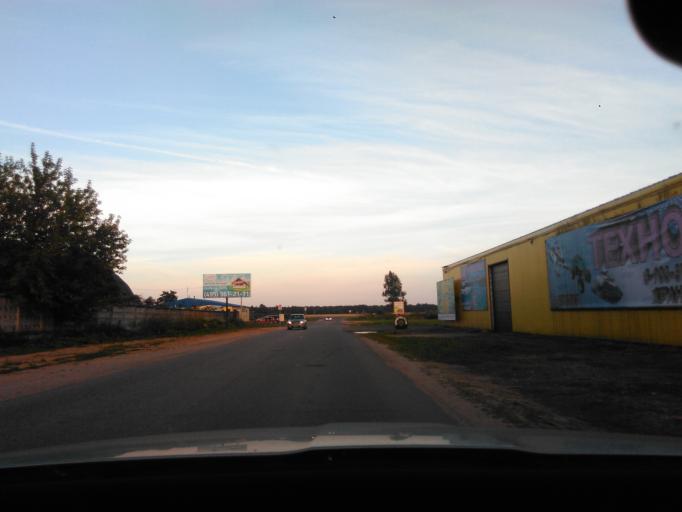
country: RU
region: Tverskaya
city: Zavidovo
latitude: 56.6080
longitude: 36.6259
